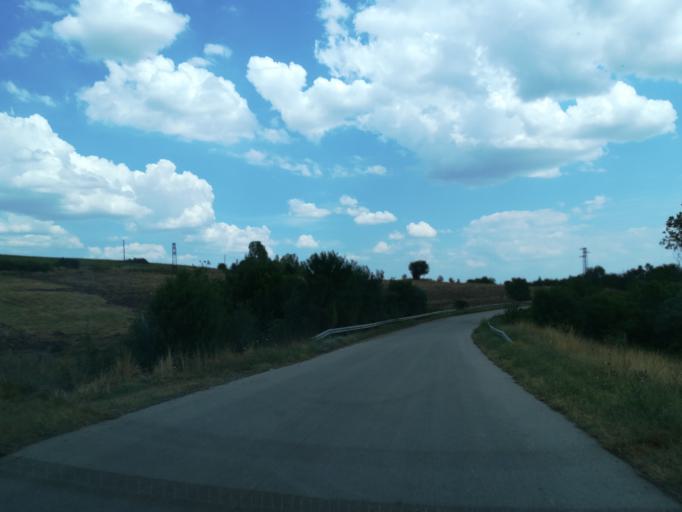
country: BG
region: Khaskovo
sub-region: Obshtina Mineralni Bani
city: Mineralni Bani
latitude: 41.9823
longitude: 25.1651
